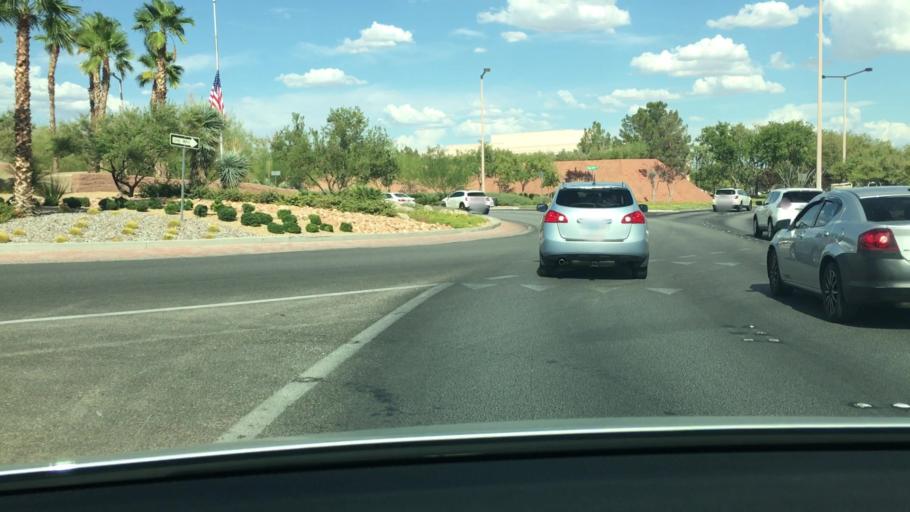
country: US
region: Nevada
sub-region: Clark County
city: Summerlin South
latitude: 36.1892
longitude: -115.3039
